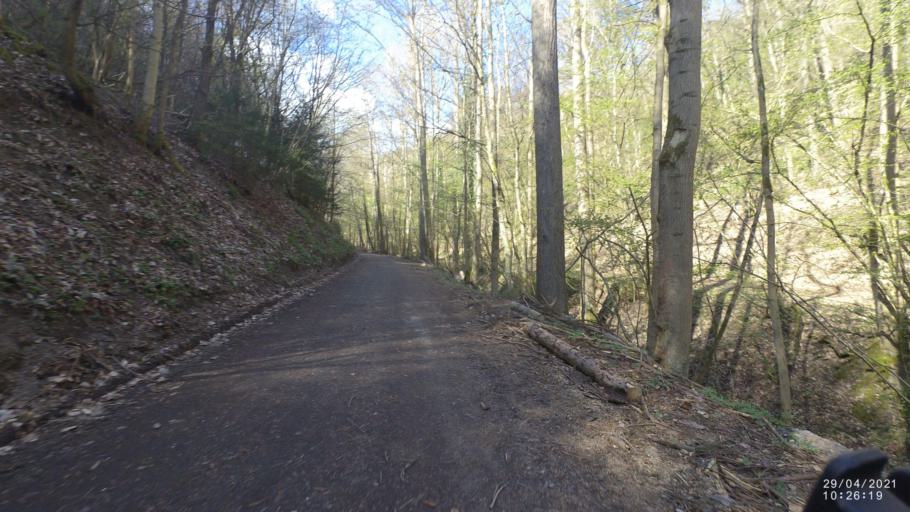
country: DE
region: Rheinland-Pfalz
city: Sankt Johann
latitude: 50.3351
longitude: 7.2002
